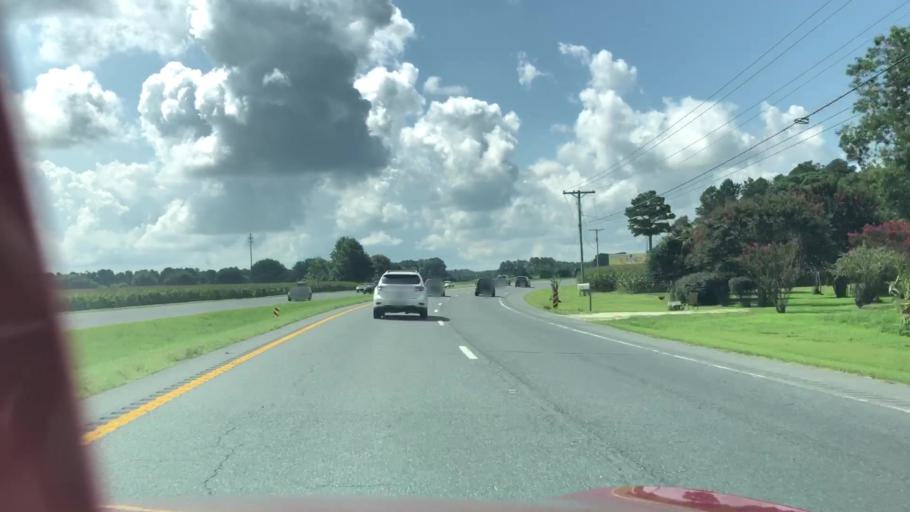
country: US
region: Virginia
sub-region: Accomack County
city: Wattsville
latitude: 37.8623
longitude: -75.5573
